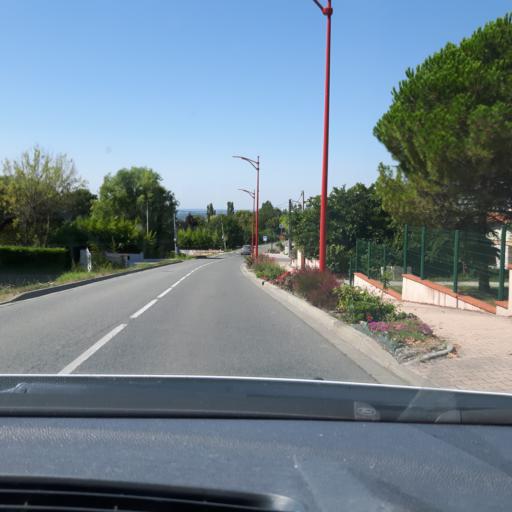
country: FR
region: Midi-Pyrenees
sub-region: Departement de la Haute-Garonne
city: Bouloc
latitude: 43.7797
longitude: 1.4016
